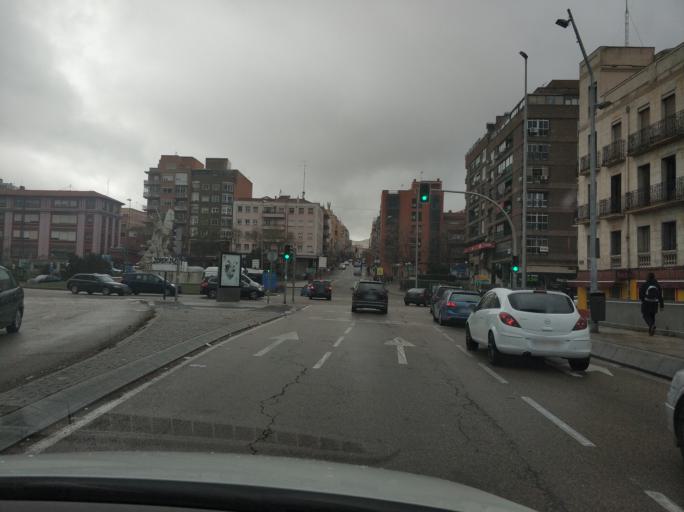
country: ES
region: Madrid
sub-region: Provincia de Madrid
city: Usera
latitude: 40.3886
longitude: -3.6990
